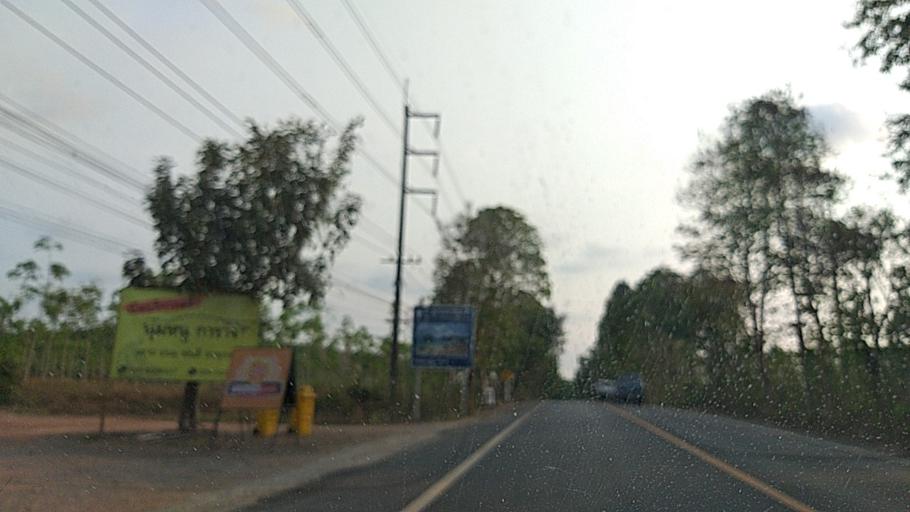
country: TH
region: Trat
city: Khao Saming
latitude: 12.3372
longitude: 102.3713
